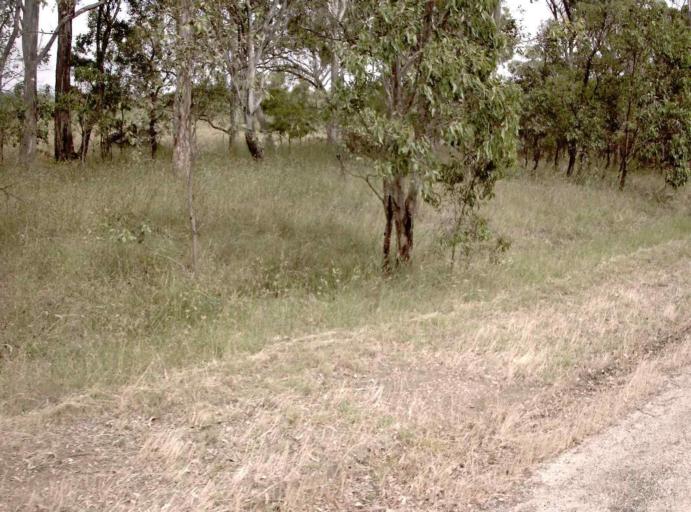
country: AU
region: Victoria
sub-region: Wellington
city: Sale
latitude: -37.8999
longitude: 147.0734
